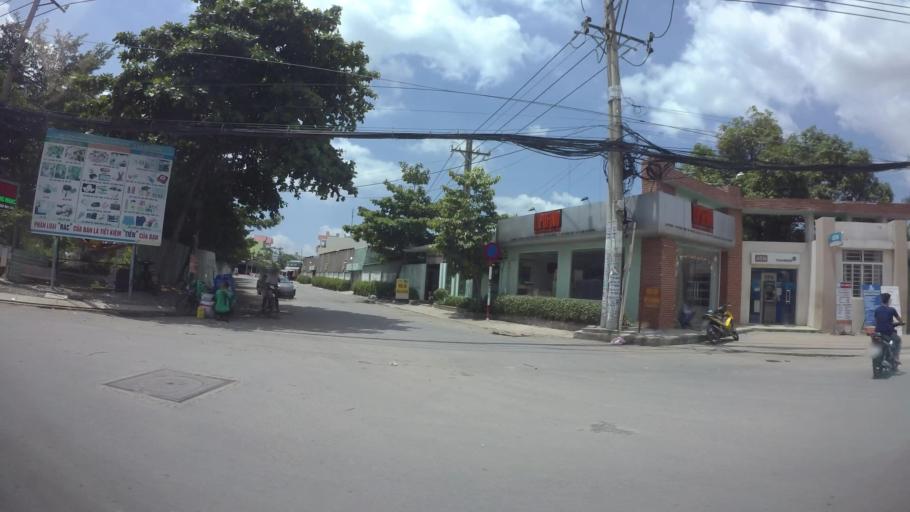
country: VN
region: Ho Chi Minh City
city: Quan Chin
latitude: 10.8275
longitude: 106.7711
